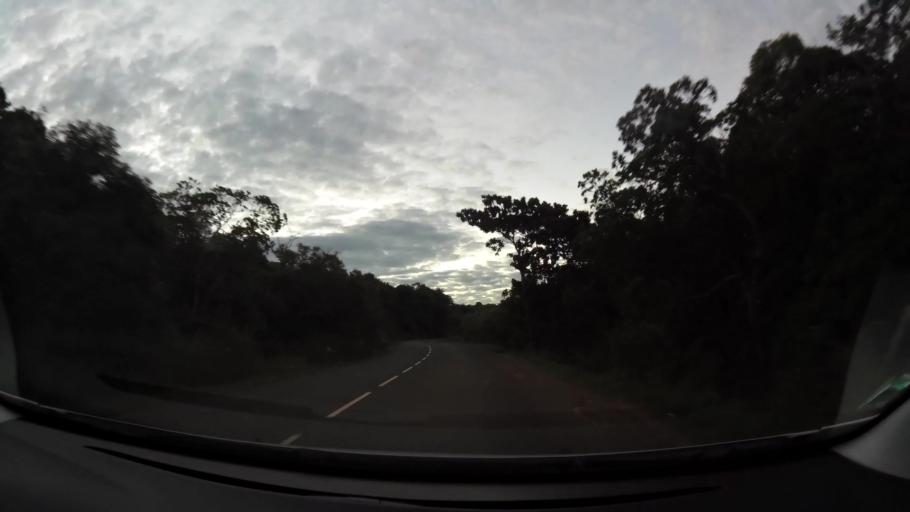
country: YT
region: Bandraboua
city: Bandraboua
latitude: -12.7305
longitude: 45.1305
